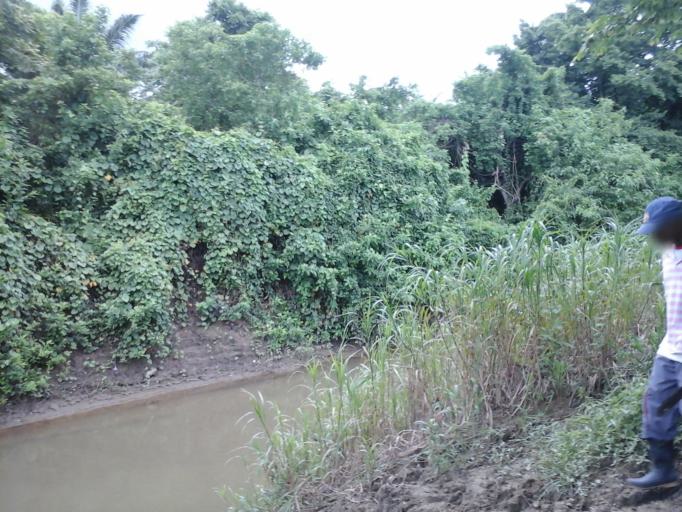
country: CO
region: Bolivar
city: San Pablo
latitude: 10.1570
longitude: -75.2737
